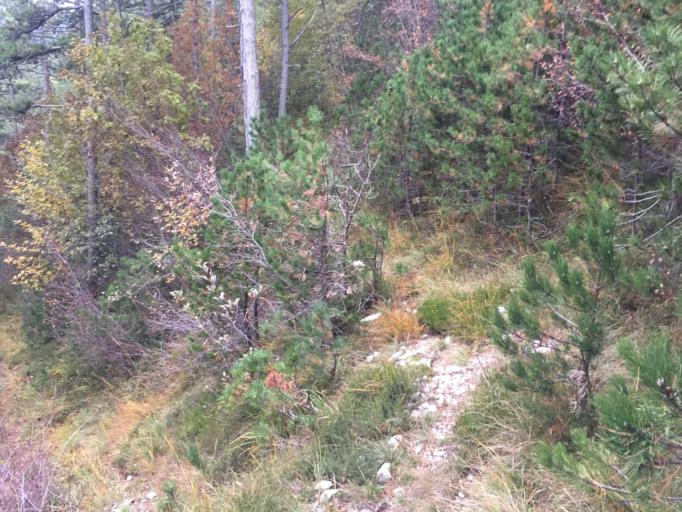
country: IT
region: Friuli Venezia Giulia
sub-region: Provincia di Udine
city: Chiusaforte
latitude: 46.4176
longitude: 13.3056
